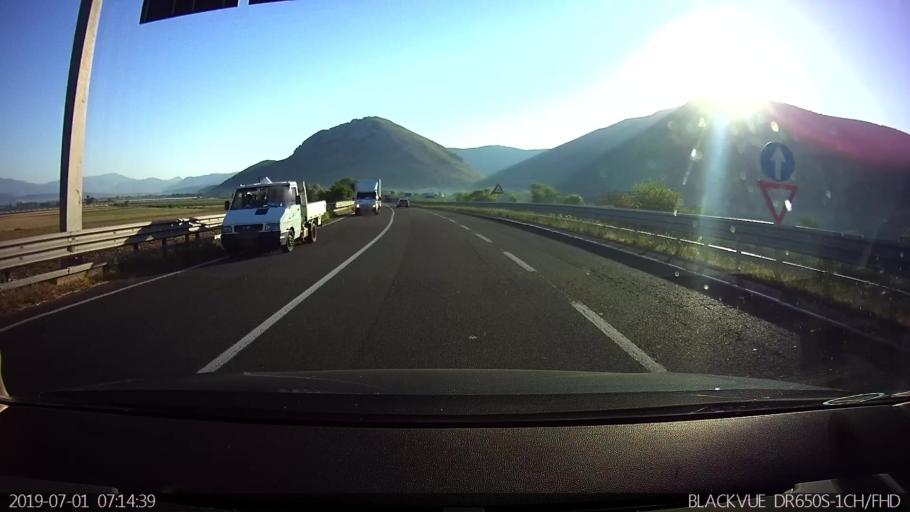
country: IT
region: Latium
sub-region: Provincia di Latina
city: Borgo Hermada
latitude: 41.3239
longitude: 13.1867
